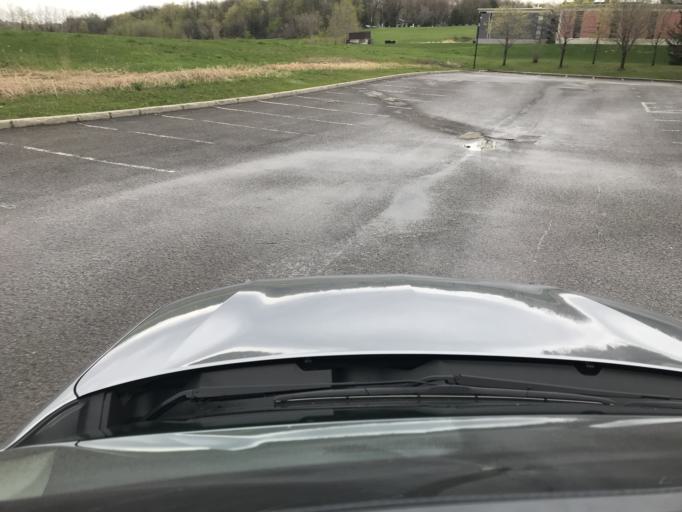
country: CA
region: Quebec
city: L'Ancienne-Lorette
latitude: 46.7927
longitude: -71.2839
